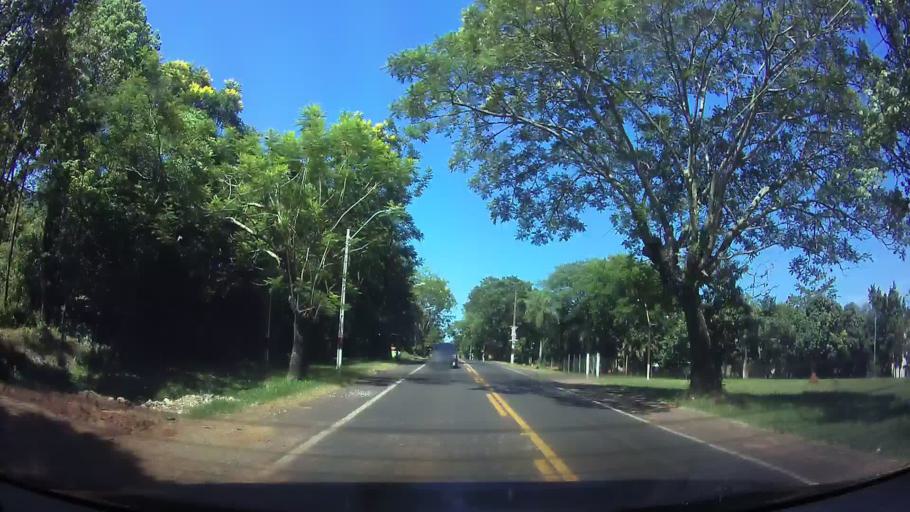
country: PY
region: Central
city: Aregua
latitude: -25.3284
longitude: -57.3987
